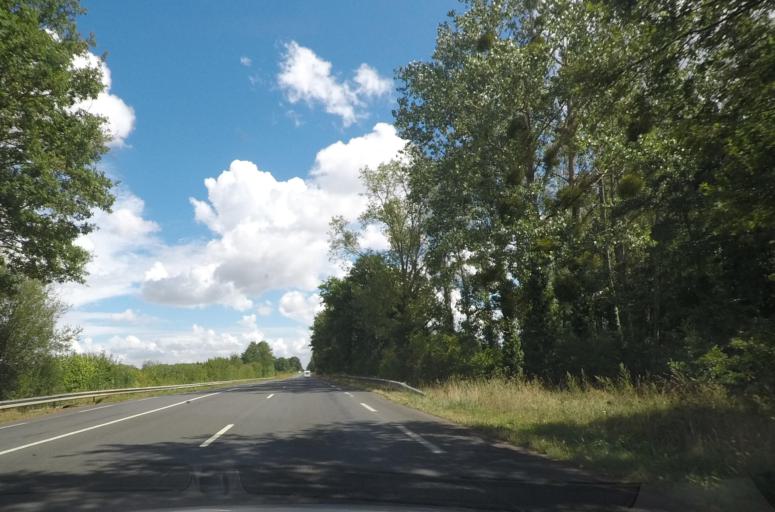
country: FR
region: Pays de la Loire
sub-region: Departement de la Sarthe
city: Guecelard
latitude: 47.8826
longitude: 0.1358
